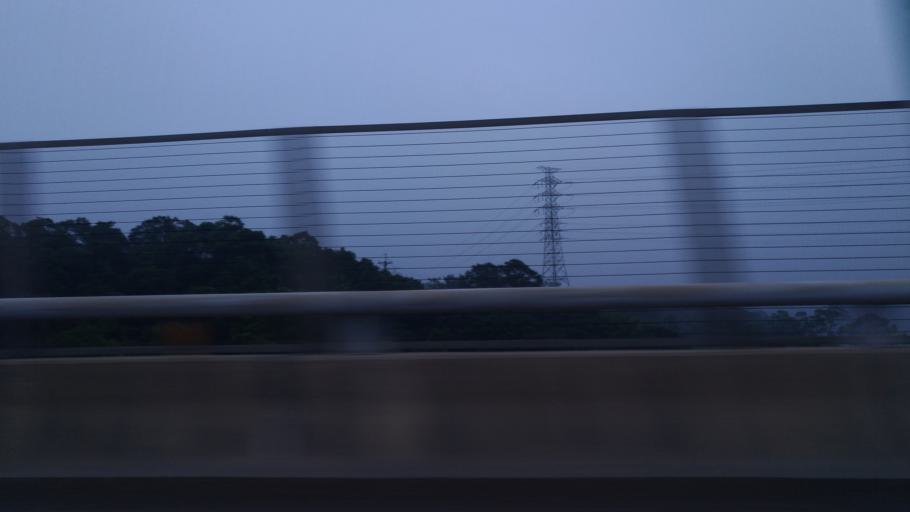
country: TW
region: Taiwan
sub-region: Hsinchu
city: Hsinchu
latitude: 24.7533
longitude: 120.9488
